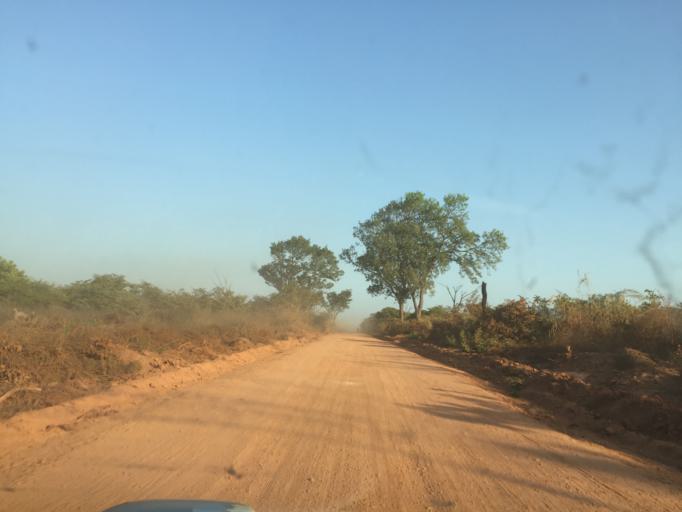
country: GW
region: Oio
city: Farim
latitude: 12.5311
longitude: -15.2737
